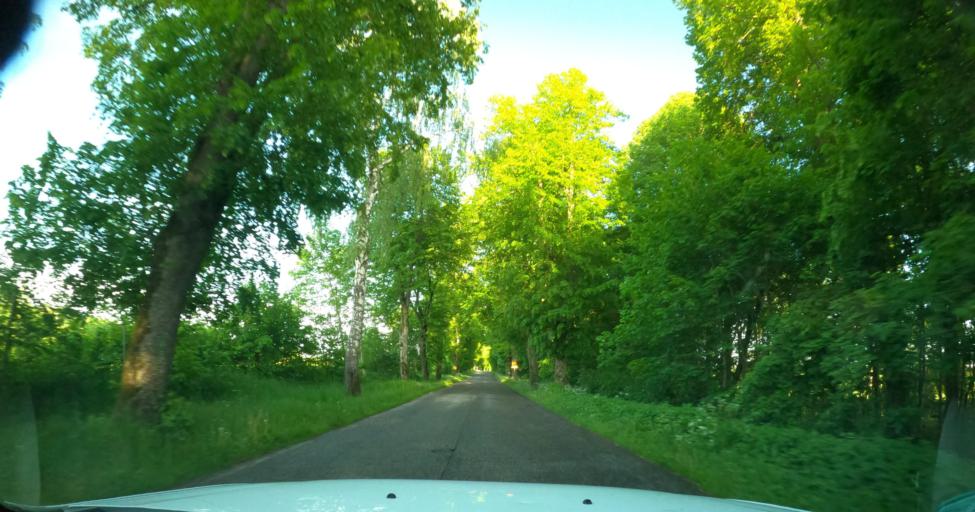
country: PL
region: Warmian-Masurian Voivodeship
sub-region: Powiat braniewski
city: Pieniezno
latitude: 54.2509
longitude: 20.0113
